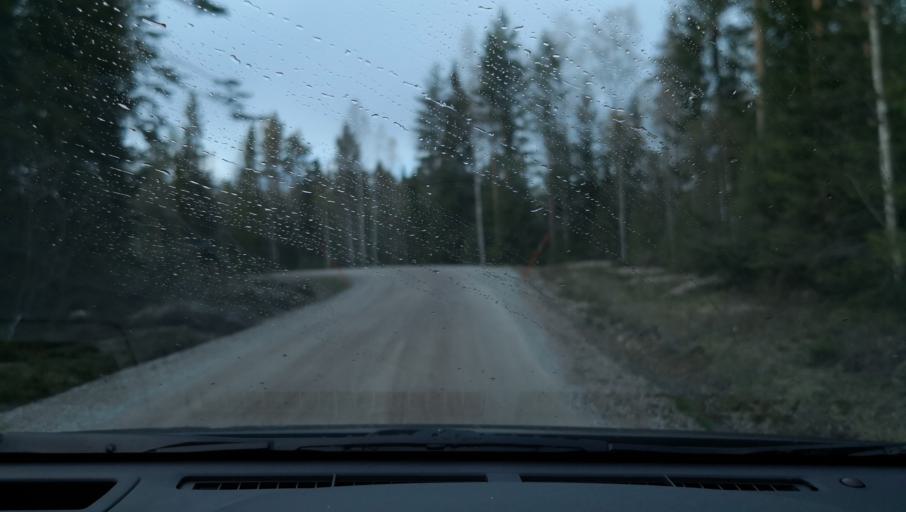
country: SE
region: Dalarna
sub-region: Saters Kommun
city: Saeter
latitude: 60.1768
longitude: 15.7253
